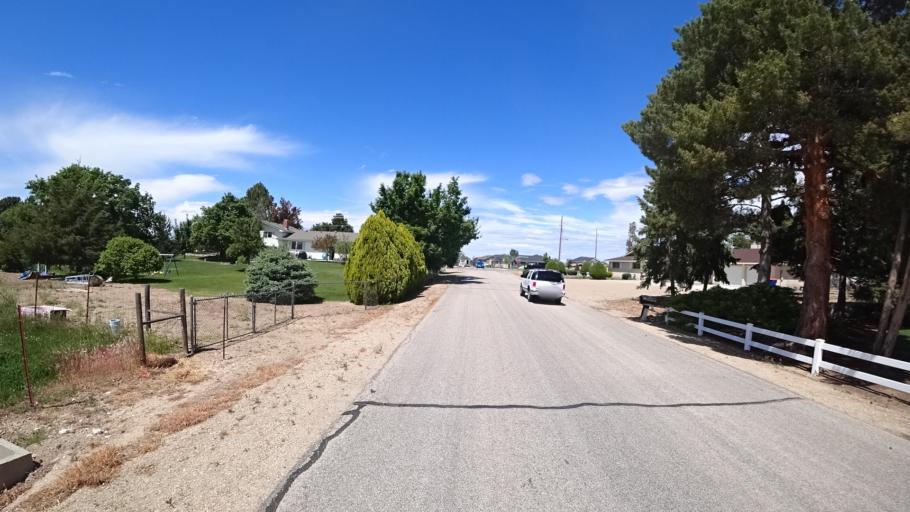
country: US
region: Idaho
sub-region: Ada County
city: Meridian
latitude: 43.5751
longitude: -116.3465
